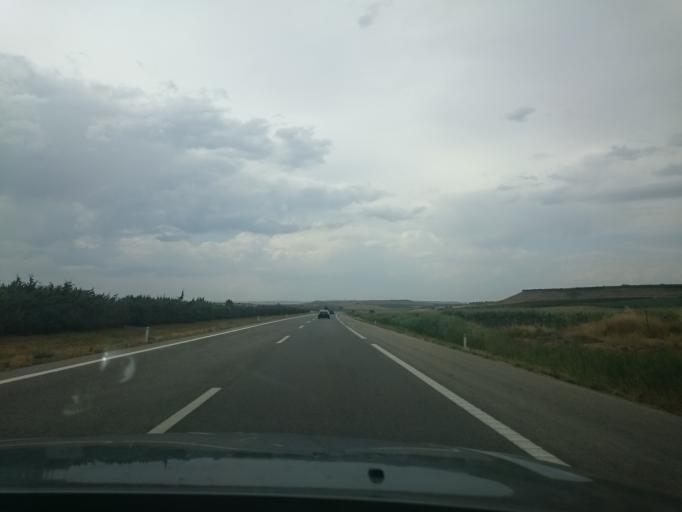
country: ES
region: Navarre
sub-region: Provincia de Navarra
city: Fontellas
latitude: 41.9973
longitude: -1.5811
